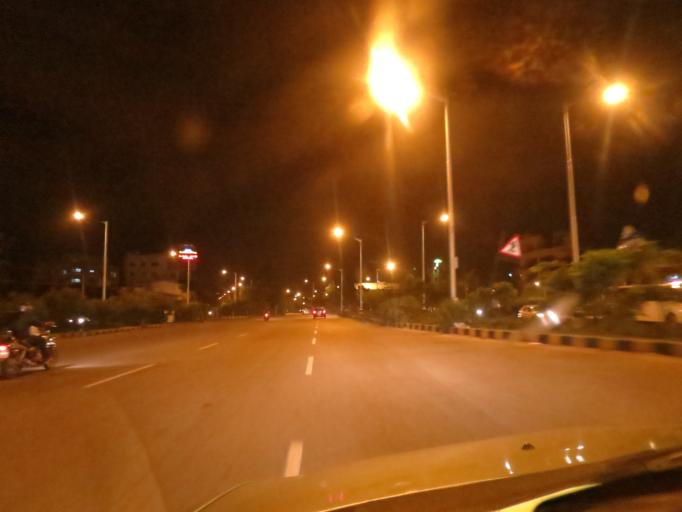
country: IN
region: Karnataka
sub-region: Bangalore Urban
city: Bangalore
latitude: 13.0253
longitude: 77.6409
